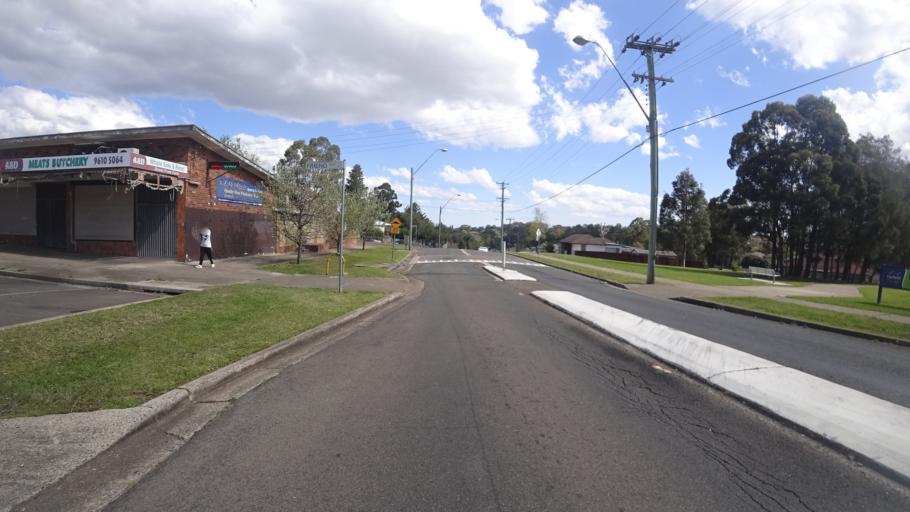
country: AU
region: New South Wales
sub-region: Fairfield
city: Cabramatta West
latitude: -33.9021
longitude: 150.9087
